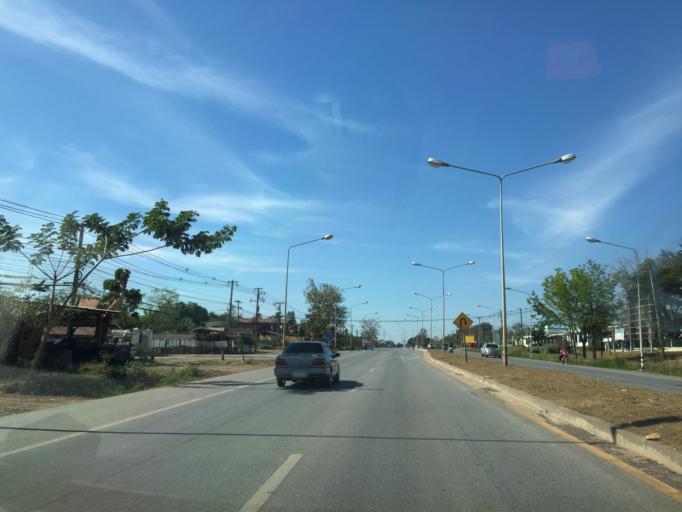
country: TH
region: Changwat Nong Bua Lamphu
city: Na Klang
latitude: 17.3057
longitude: 102.1891
